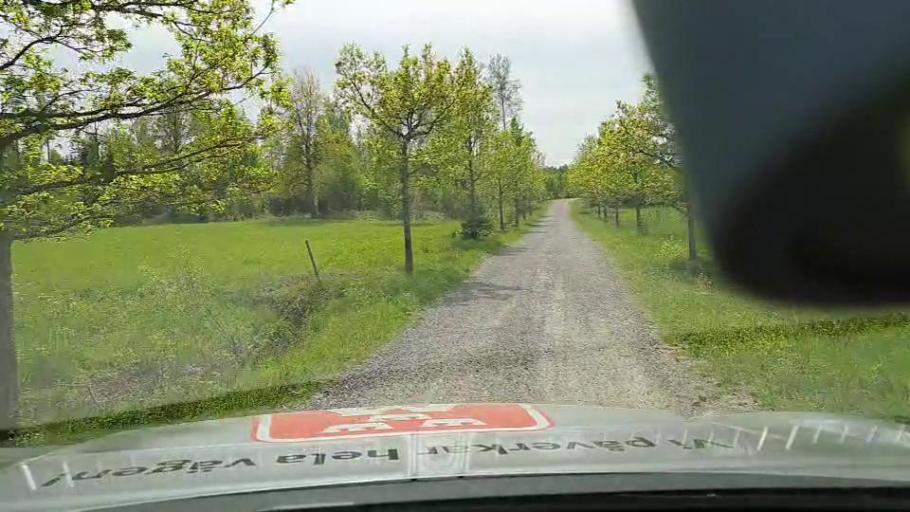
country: SE
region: Soedermanland
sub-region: Eskilstuna Kommun
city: Skogstorp
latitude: 59.2499
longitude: 16.5010
